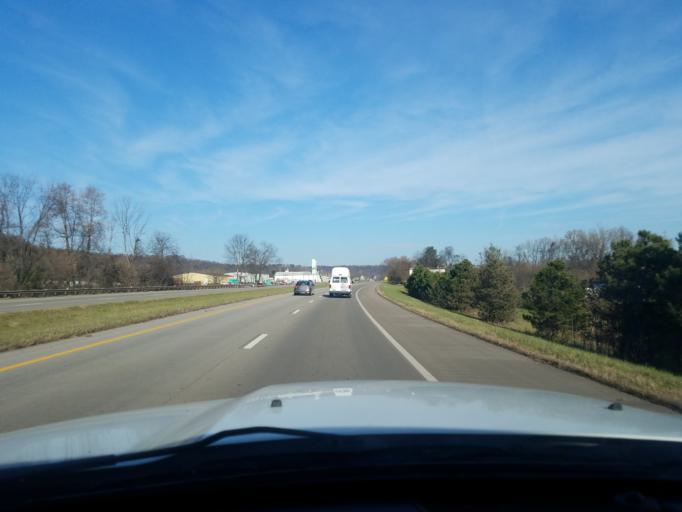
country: US
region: West Virginia
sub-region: Wood County
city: Vienna
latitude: 39.3541
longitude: -81.5513
